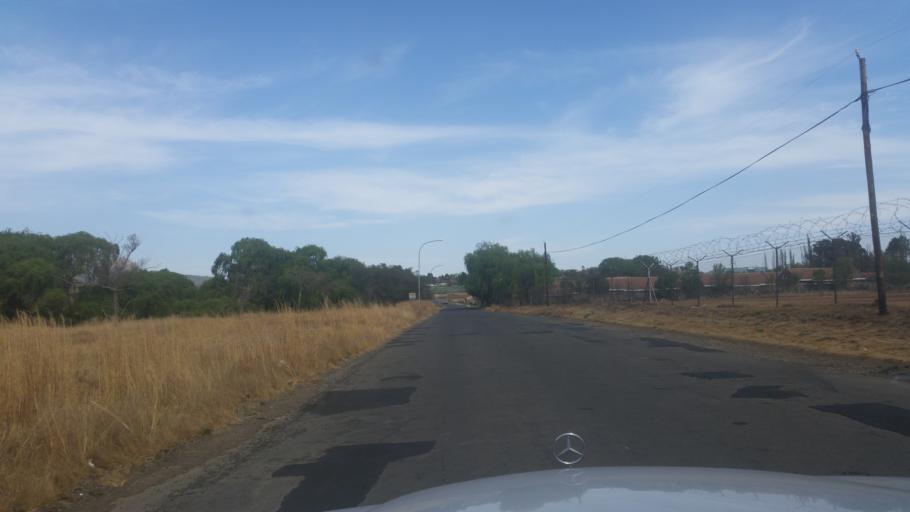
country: ZA
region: Orange Free State
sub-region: Thabo Mofutsanyana District Municipality
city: Harrismith
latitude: -28.2663
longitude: 29.1362
